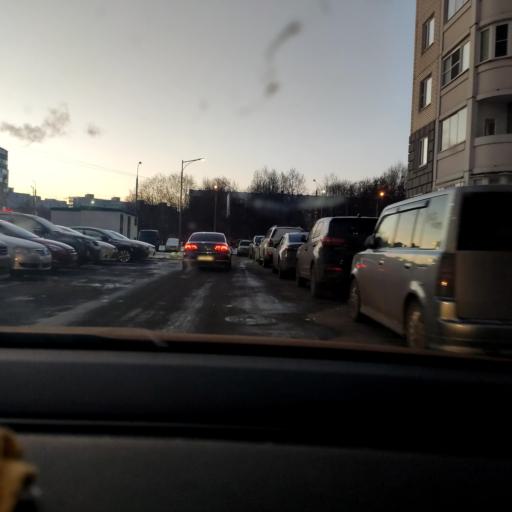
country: RU
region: Moskovskaya
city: Moskovskiy
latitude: 55.6002
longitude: 37.3569
